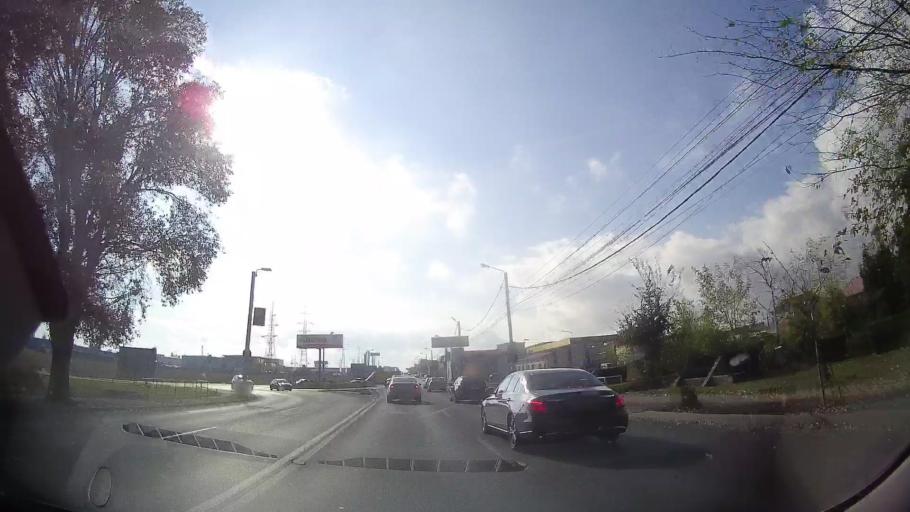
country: RO
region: Constanta
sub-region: Municipiul Constanta
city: Constanta
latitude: 44.1387
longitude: 28.6211
